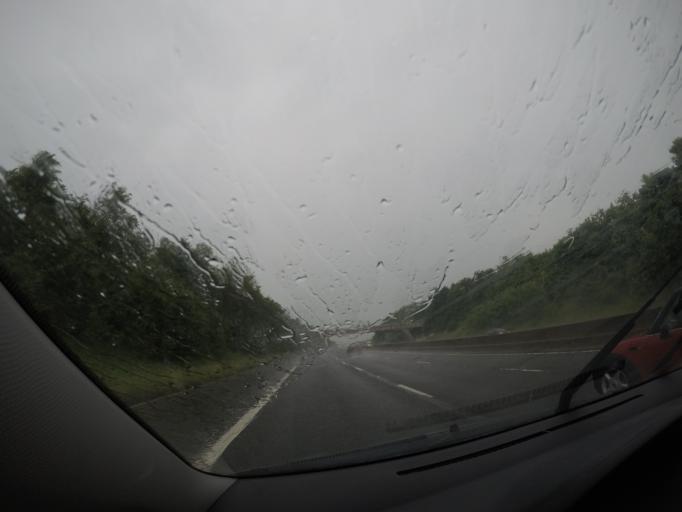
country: GB
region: England
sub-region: Cumbria
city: Penrith
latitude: 54.6624
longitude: -2.7721
